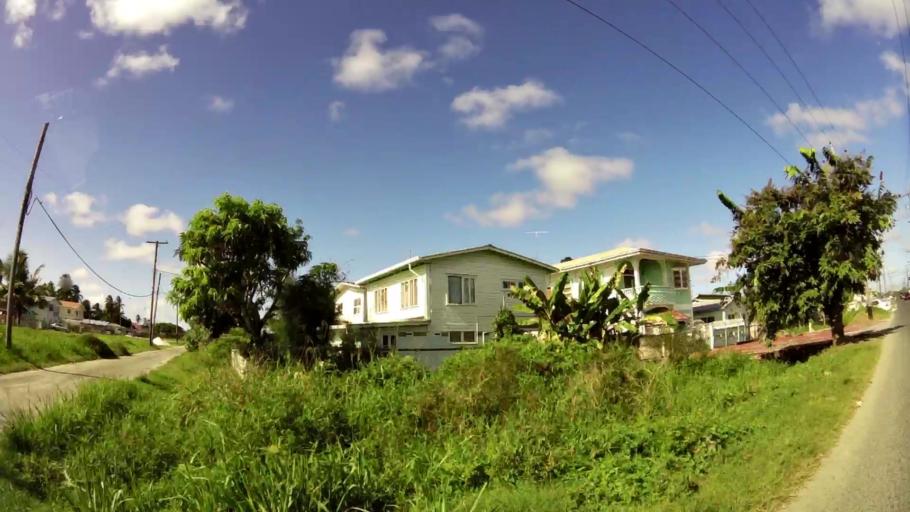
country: GY
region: Demerara-Mahaica
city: Georgetown
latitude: 6.8151
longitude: -58.1332
